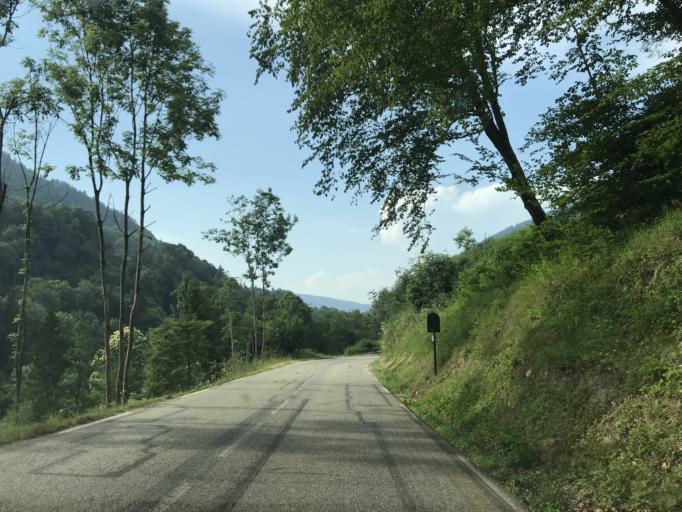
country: FR
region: Rhone-Alpes
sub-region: Departement de l'Isere
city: Allevard
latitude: 45.3646
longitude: 6.0973
